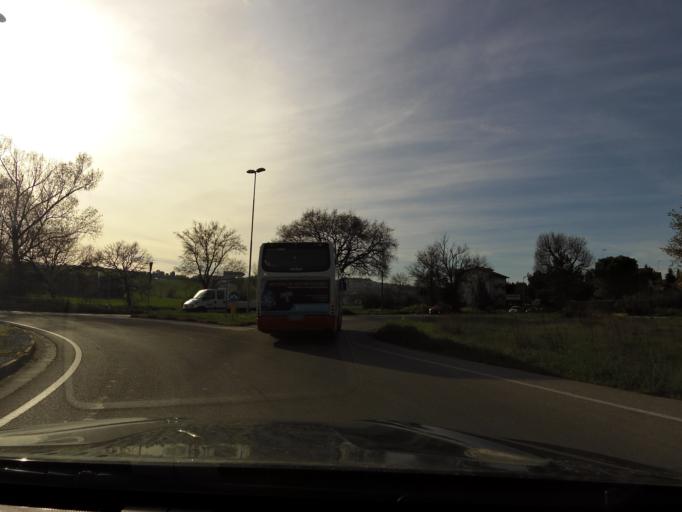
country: IT
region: The Marches
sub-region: Provincia di Ancona
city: Villa Musone
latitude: 43.4584
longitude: 13.5835
